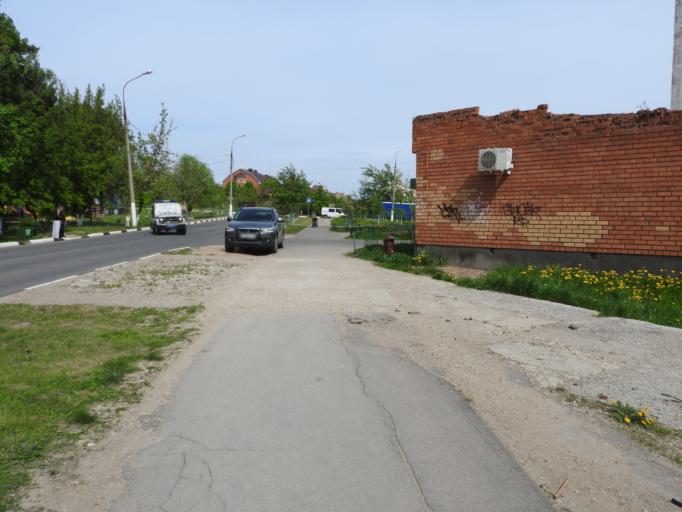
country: RU
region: Moskovskaya
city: Odintsovo
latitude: 55.6668
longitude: 37.2944
